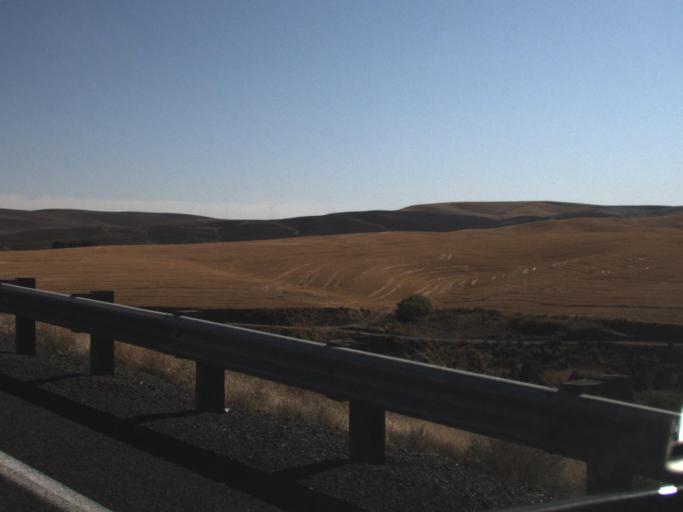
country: US
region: Washington
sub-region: Walla Walla County
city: Garrett
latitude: 46.2881
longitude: -118.4961
